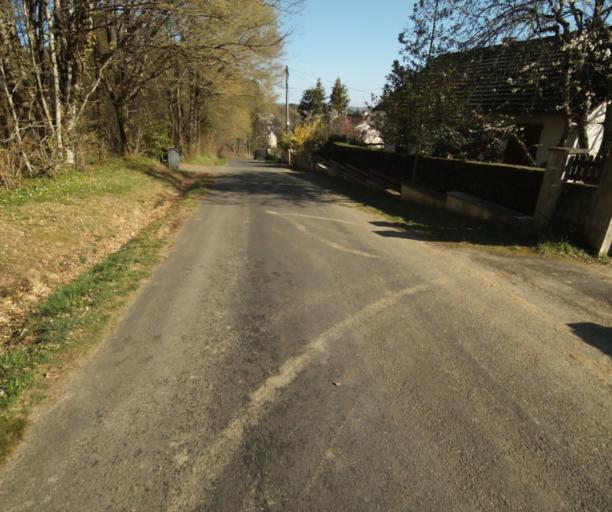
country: FR
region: Limousin
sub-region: Departement de la Correze
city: Chameyrat
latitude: 45.2881
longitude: 1.7079
